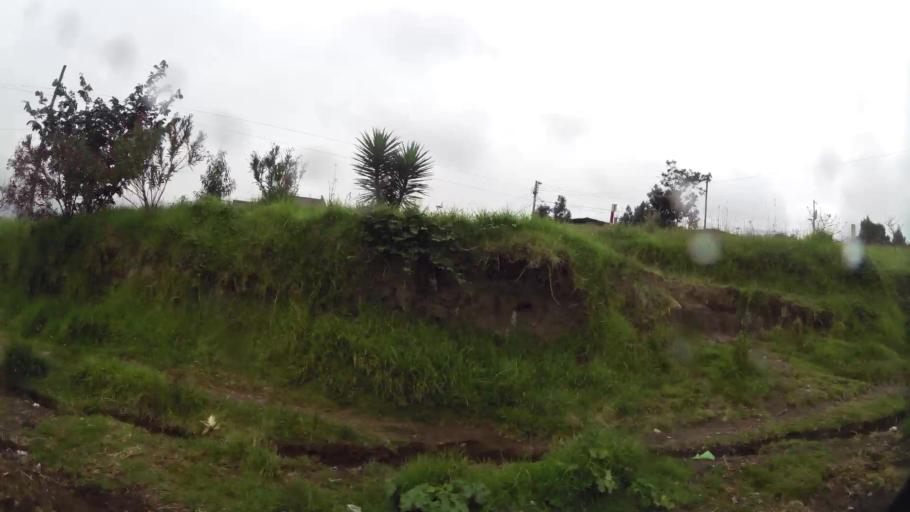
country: EC
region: Pichincha
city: Sangolqui
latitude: -0.2784
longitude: -78.4747
